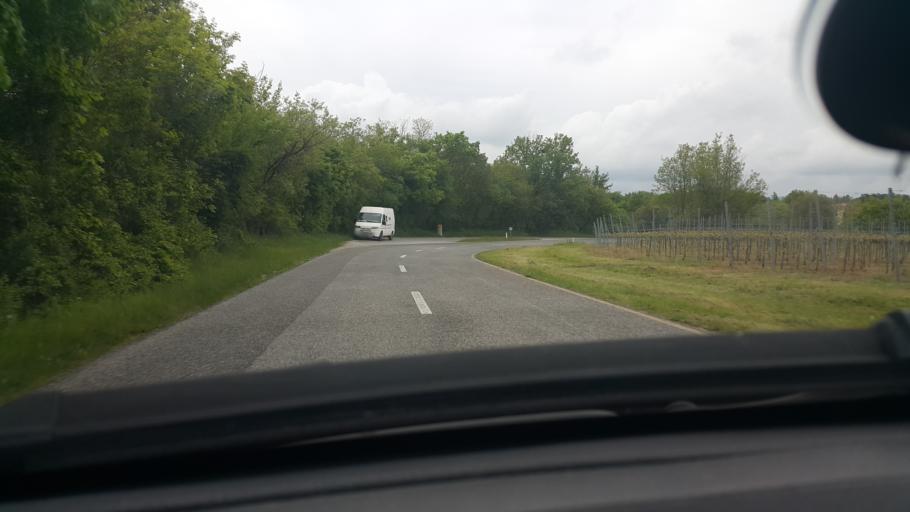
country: SI
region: Komen
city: Komen
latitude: 45.8104
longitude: 13.7548
